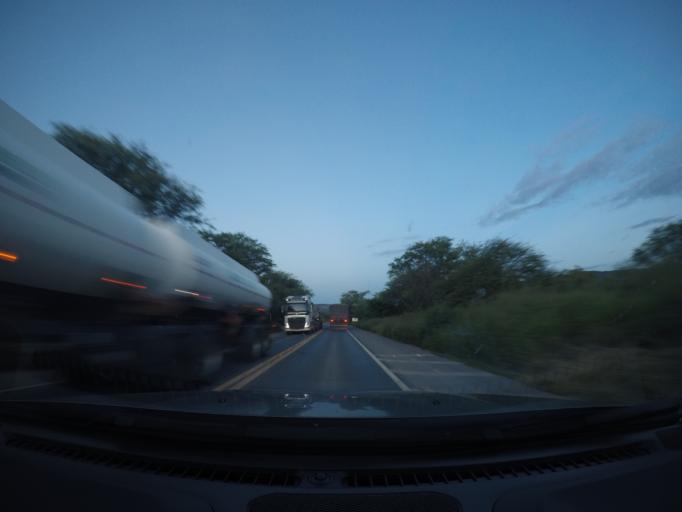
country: BR
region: Bahia
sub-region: Seabra
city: Seabra
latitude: -12.4877
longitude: -41.7281
